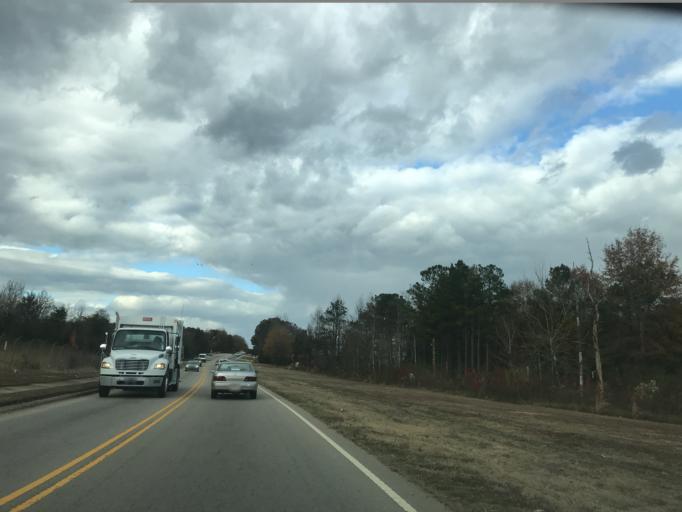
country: US
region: North Carolina
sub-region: Wake County
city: Raleigh
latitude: 35.7903
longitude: -78.5607
